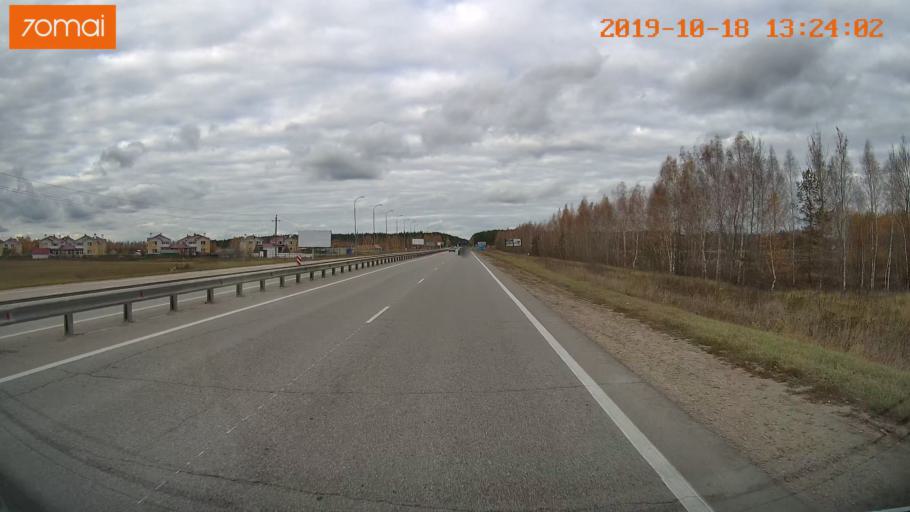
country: RU
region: Rjazan
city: Polyany
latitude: 54.7250
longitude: 39.8468
